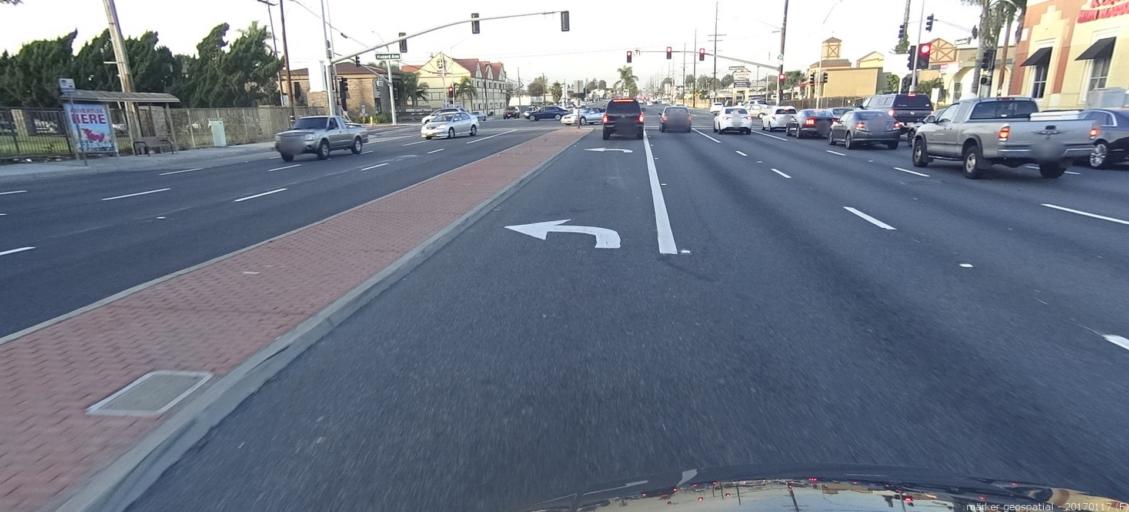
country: US
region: California
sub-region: Orange County
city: Midway City
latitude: 33.7514
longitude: -117.9895
